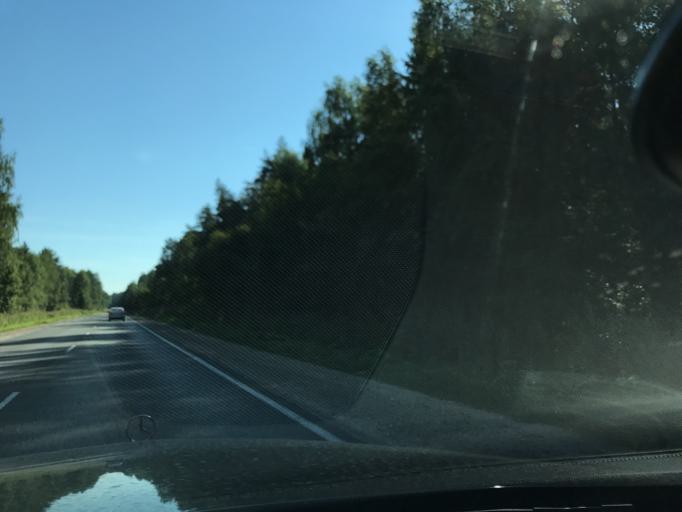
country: RU
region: Vladimir
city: Kirzhach
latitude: 56.1363
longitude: 38.7959
